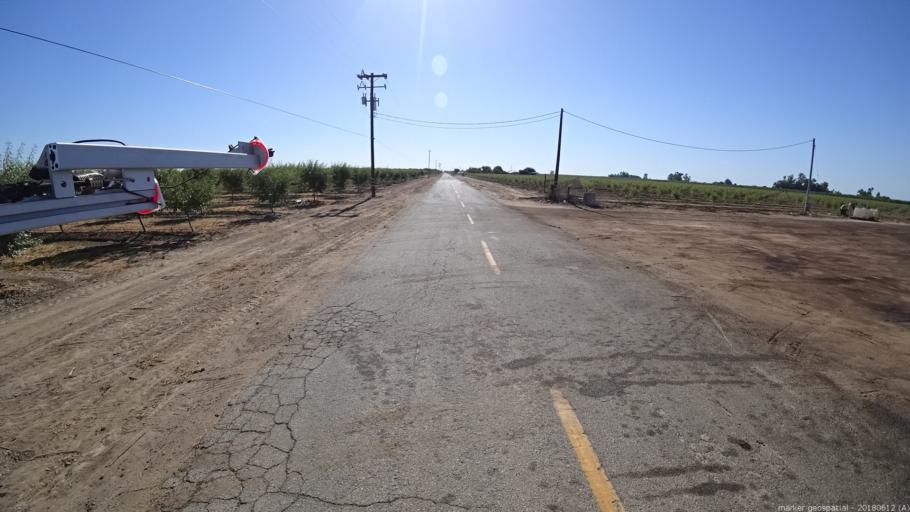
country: US
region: California
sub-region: Madera County
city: Fairmead
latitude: 37.0110
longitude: -120.2639
